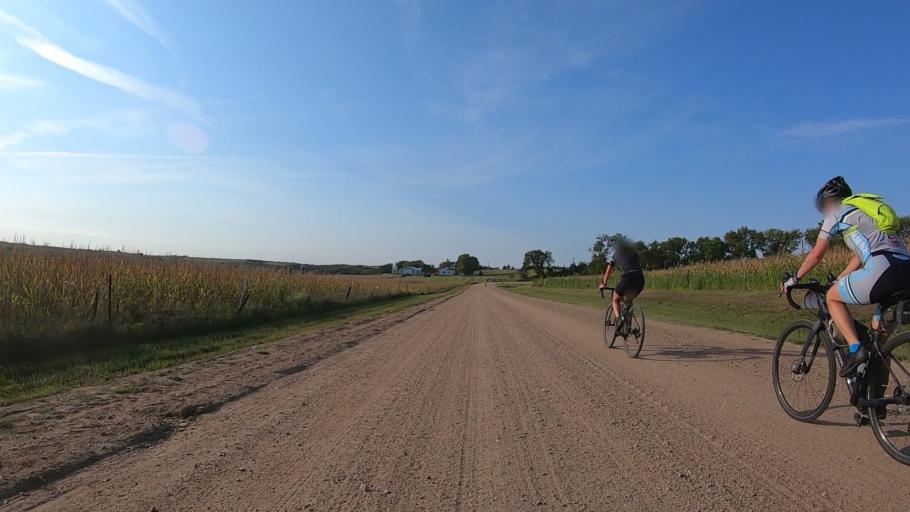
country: US
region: Kansas
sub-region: Marshall County
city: Blue Rapids
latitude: 39.6773
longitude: -96.7839
